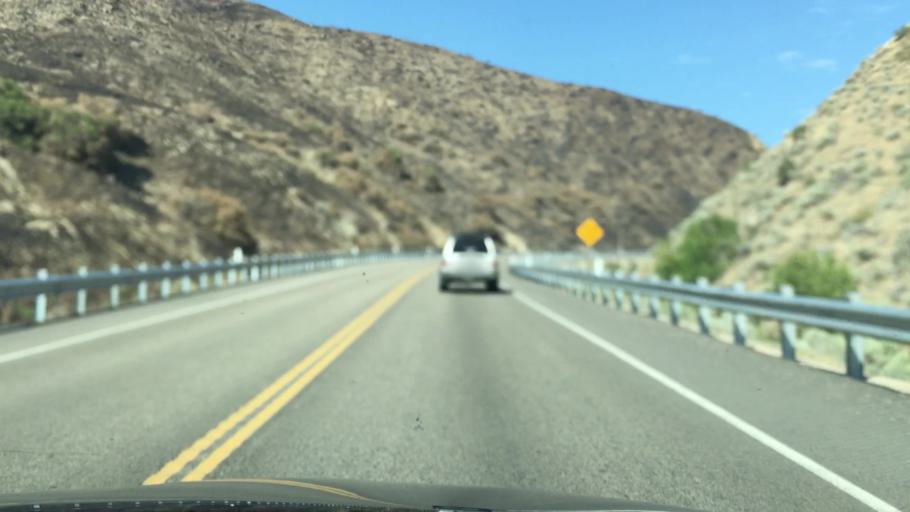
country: US
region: Idaho
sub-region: Ada County
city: Eagle
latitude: 43.7592
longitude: -116.2742
